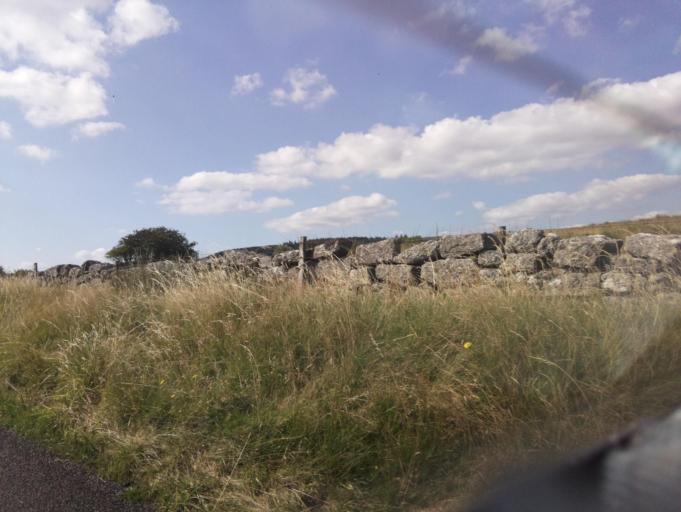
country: GB
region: England
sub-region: Devon
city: Yelverton
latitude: 50.5575
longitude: -3.9606
